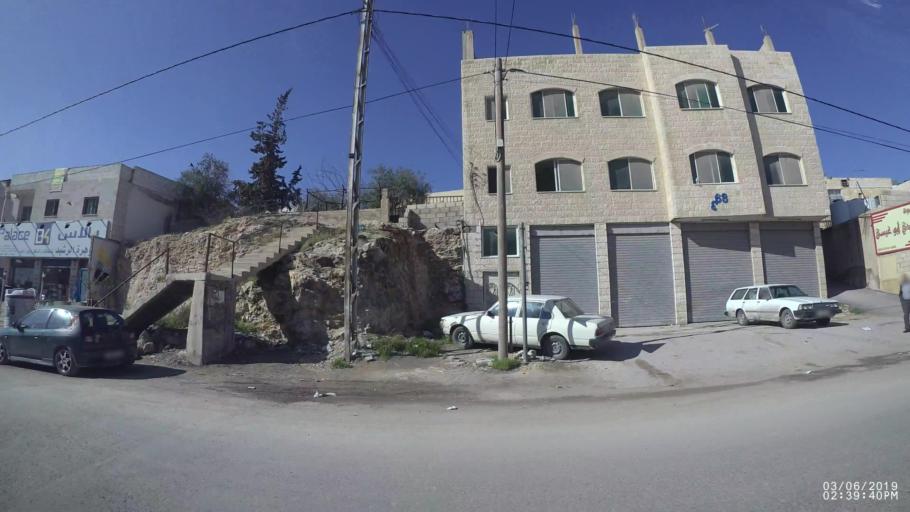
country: JO
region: Zarqa
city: Russeifa
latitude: 32.0279
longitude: 36.0169
